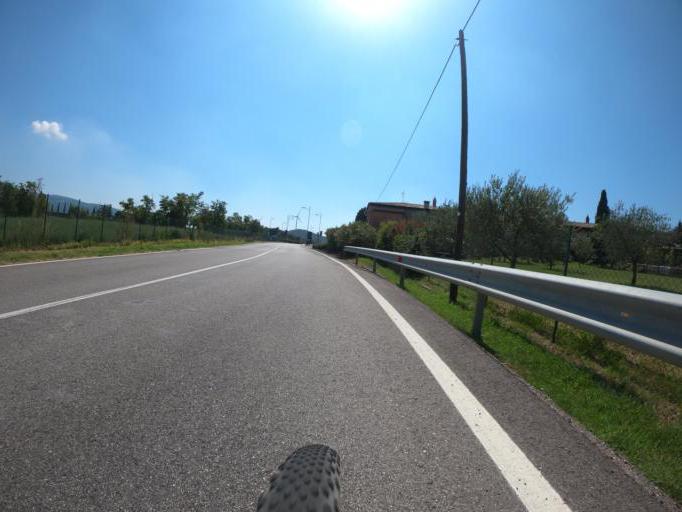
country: IT
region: Veneto
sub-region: Provincia di Verona
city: Rivoli Veronese
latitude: 45.5751
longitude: 10.8039
